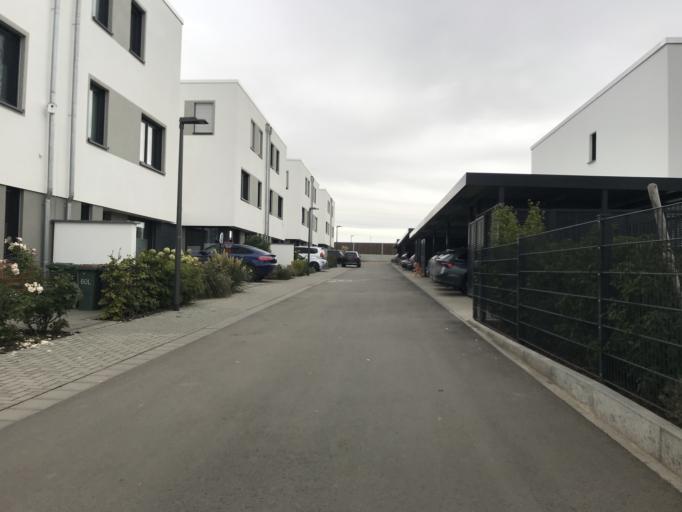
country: DE
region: Rheinland-Pfalz
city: Mainz
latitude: 49.9537
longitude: 8.2692
